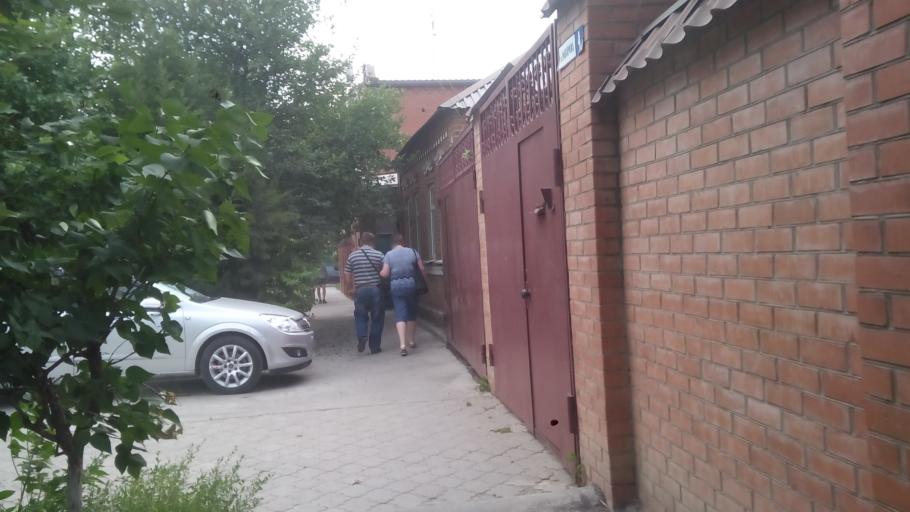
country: RU
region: Rostov
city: Rostov-na-Donu
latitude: 47.2280
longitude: 39.6364
